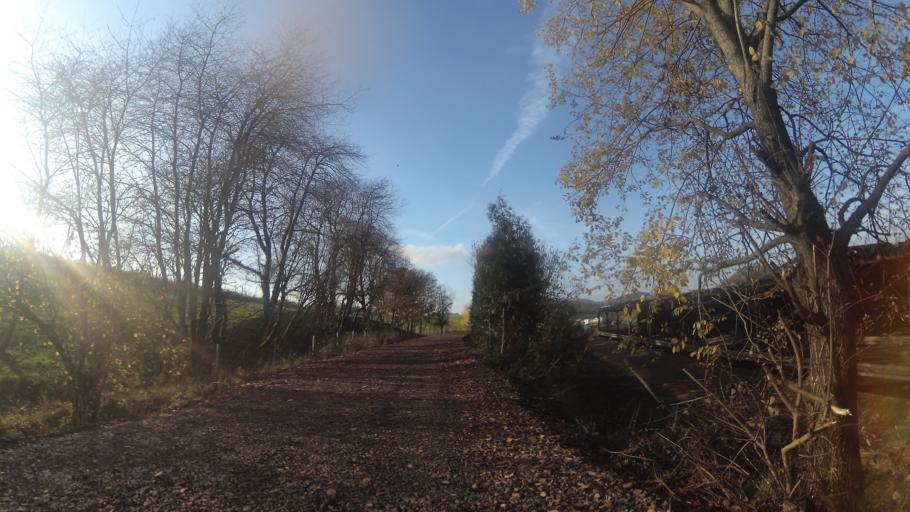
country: DE
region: Rheinland-Pfalz
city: Hahnweiler
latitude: 49.5496
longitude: 7.1865
